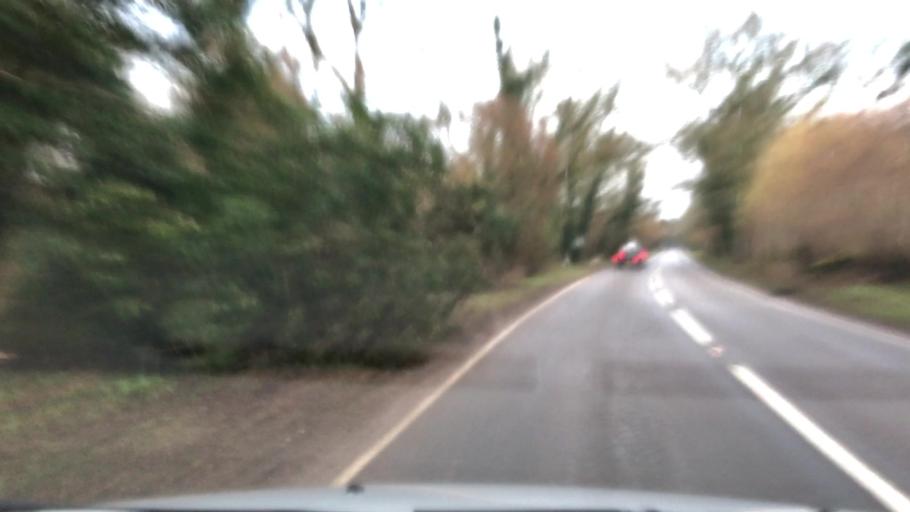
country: GB
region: England
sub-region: Hampshire
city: Alton
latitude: 51.1947
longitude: -0.9835
